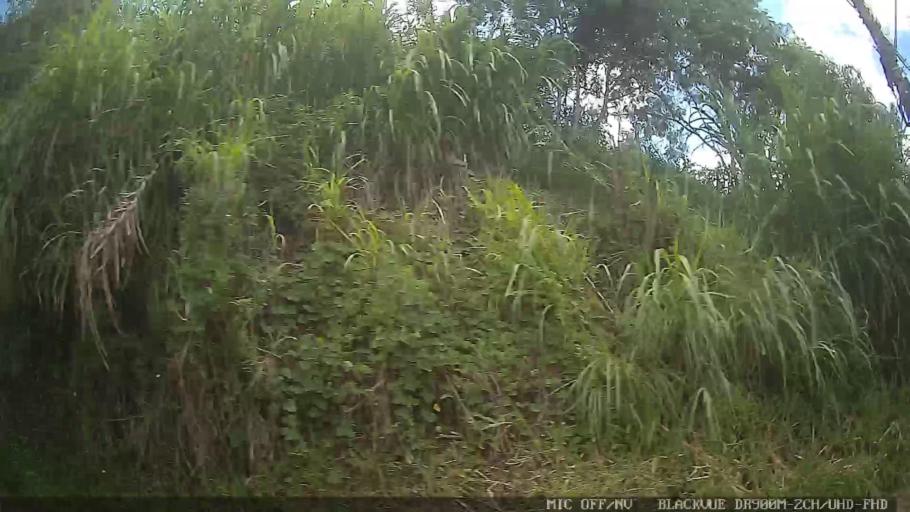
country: BR
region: Sao Paulo
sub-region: Atibaia
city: Atibaia
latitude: -23.0438
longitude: -46.4960
